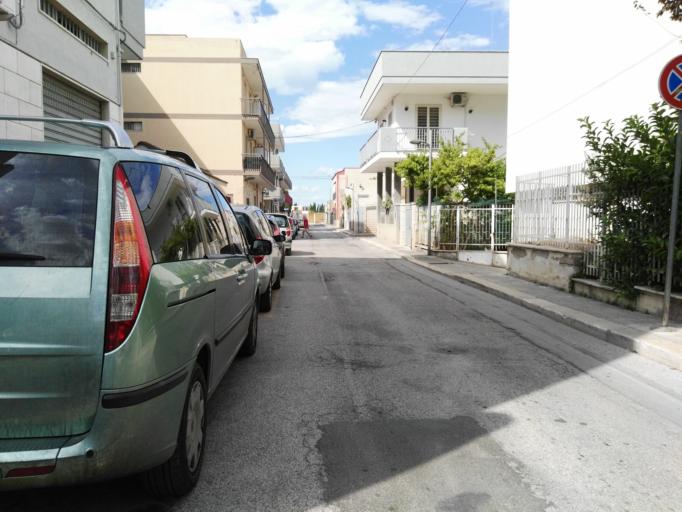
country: IT
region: Apulia
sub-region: Provincia di Bari
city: Triggiano
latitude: 41.0652
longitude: 16.9181
